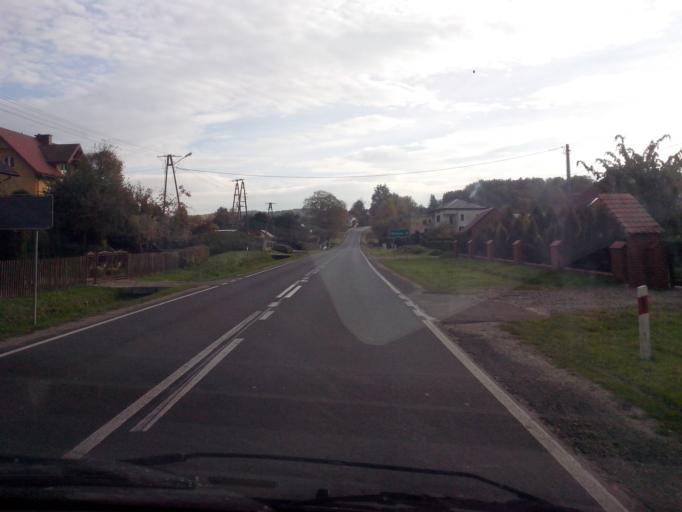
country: PL
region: Subcarpathian Voivodeship
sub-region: Powiat ropczycko-sedziszowski
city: Wielopole Skrzynskie
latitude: 49.9420
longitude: 21.6158
